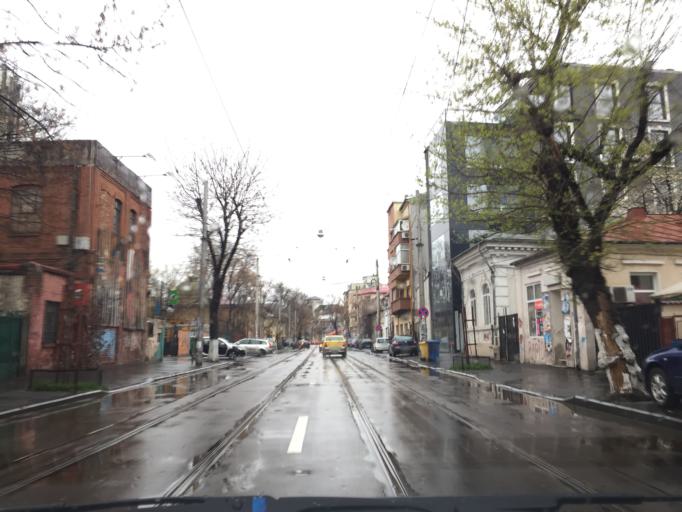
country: RO
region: Bucuresti
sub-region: Municipiul Bucuresti
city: Bucuresti
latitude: 44.4200
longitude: 26.0952
